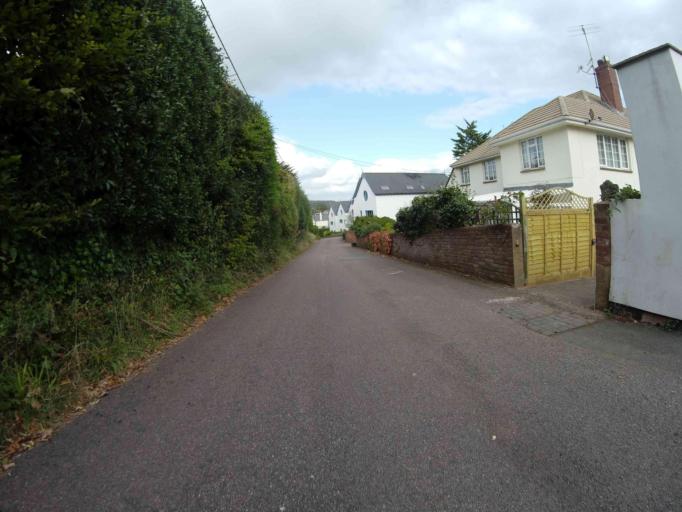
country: GB
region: England
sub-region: Devon
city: Budleigh Salterton
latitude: 50.6285
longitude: -3.3323
